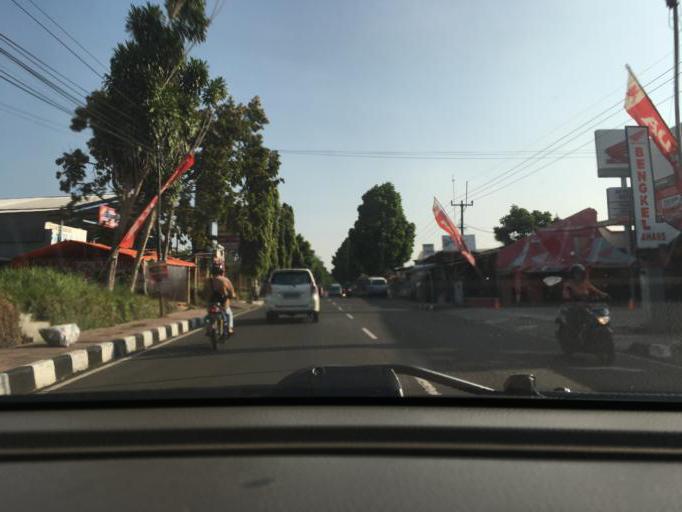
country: ID
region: West Java
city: Kuningan
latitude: -6.9519
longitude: 108.4884
